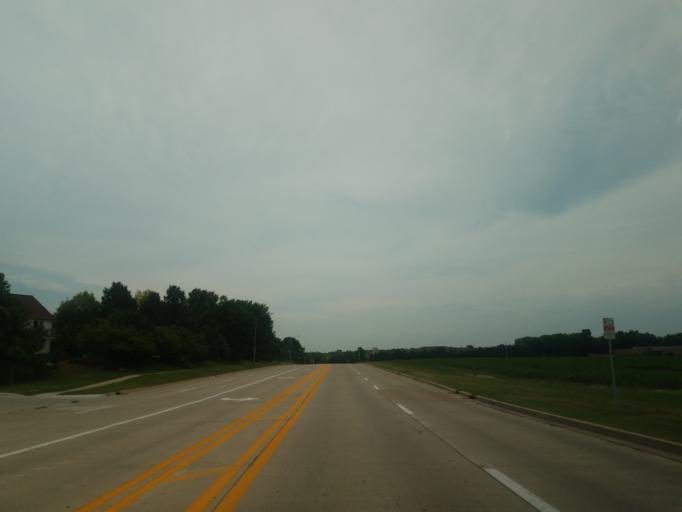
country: US
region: Illinois
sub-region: McLean County
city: Normal
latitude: 40.5098
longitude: -88.9420
